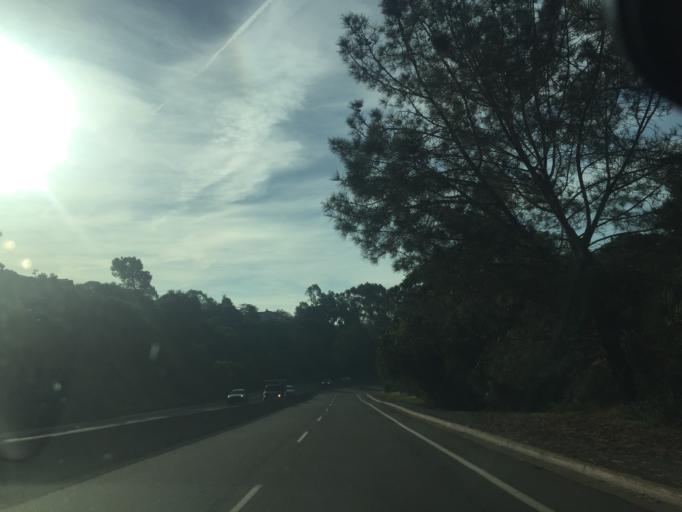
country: US
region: California
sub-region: San Diego County
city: La Jolla
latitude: 32.8633
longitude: -117.2432
